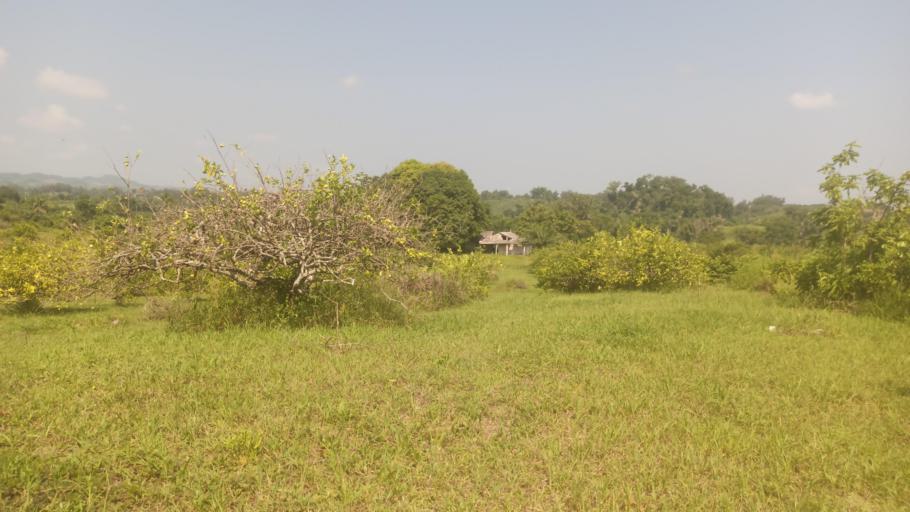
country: MX
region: Puebla
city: Espinal
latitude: 20.2270
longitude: -97.3237
